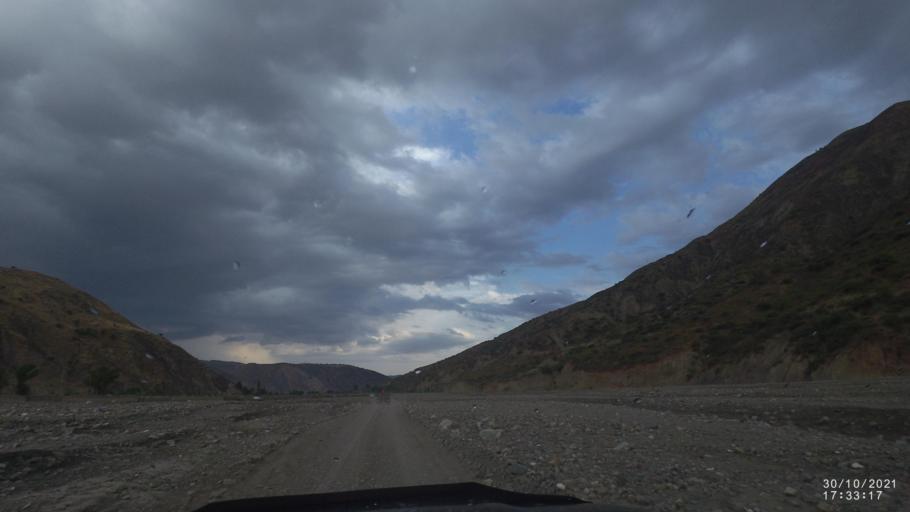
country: BO
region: Cochabamba
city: Sipe Sipe
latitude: -17.5266
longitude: -66.5824
